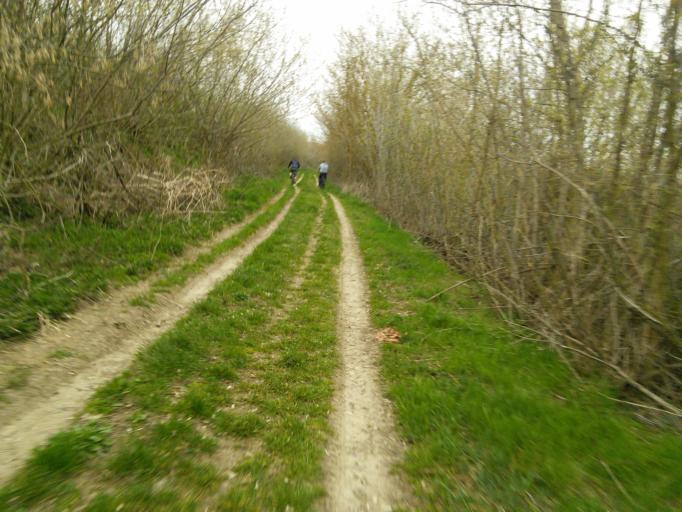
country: HU
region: Tolna
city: Dombovar
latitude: 46.4090
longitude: 18.1830
